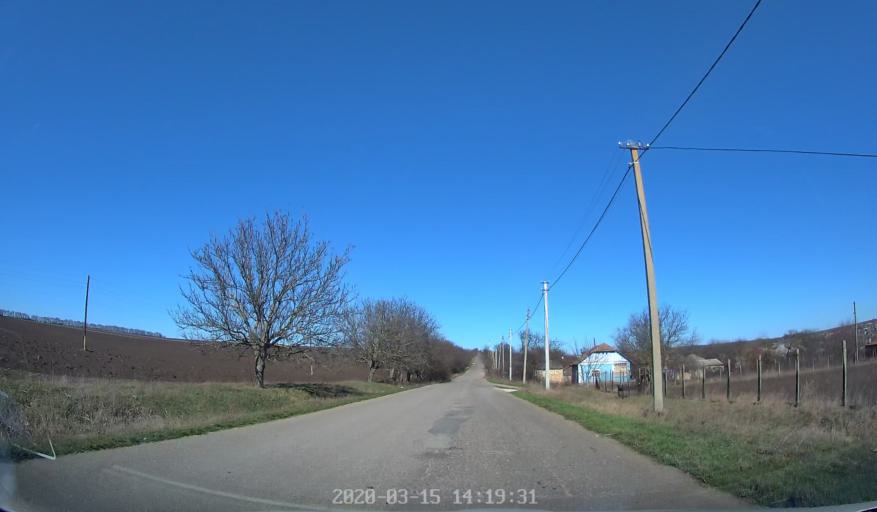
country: MD
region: Orhei
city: Orhei
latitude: 47.3049
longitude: 28.9165
